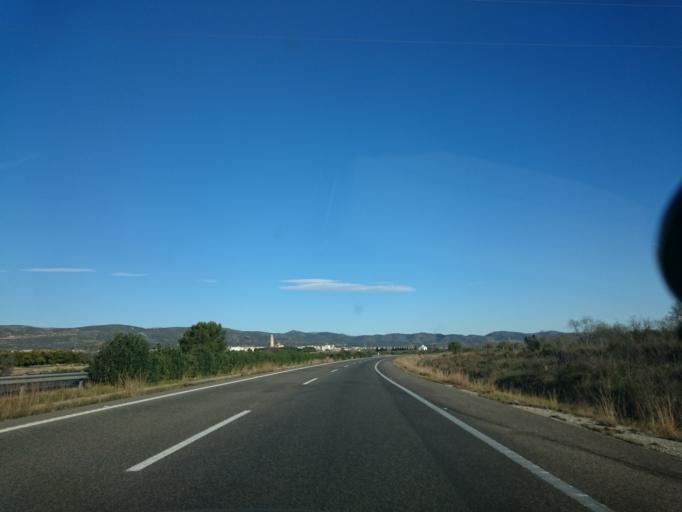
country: ES
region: Valencia
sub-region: Provincia de Castello
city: Alcala de Xivert
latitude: 40.2870
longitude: 0.2284
